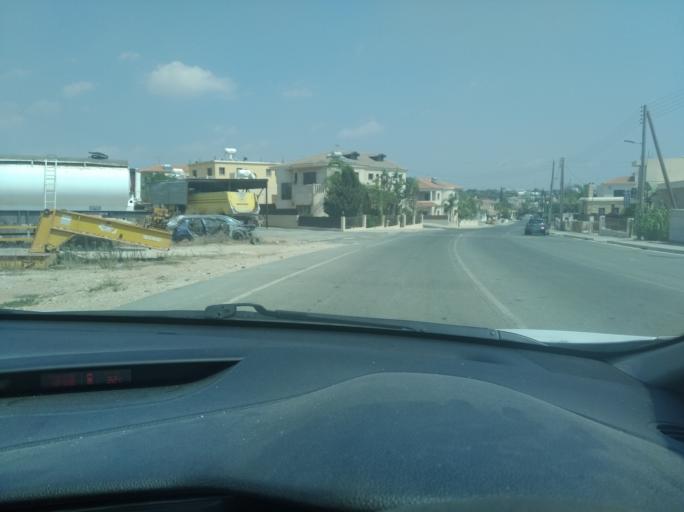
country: CY
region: Larnaka
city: Xylotymbou
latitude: 34.9938
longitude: 33.7652
